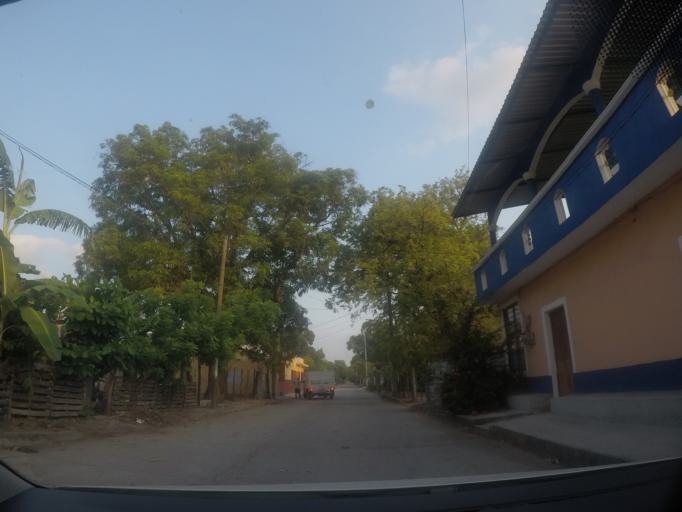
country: MX
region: Oaxaca
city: San Jeronimo Ixtepec
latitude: 16.5861
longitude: -95.2102
